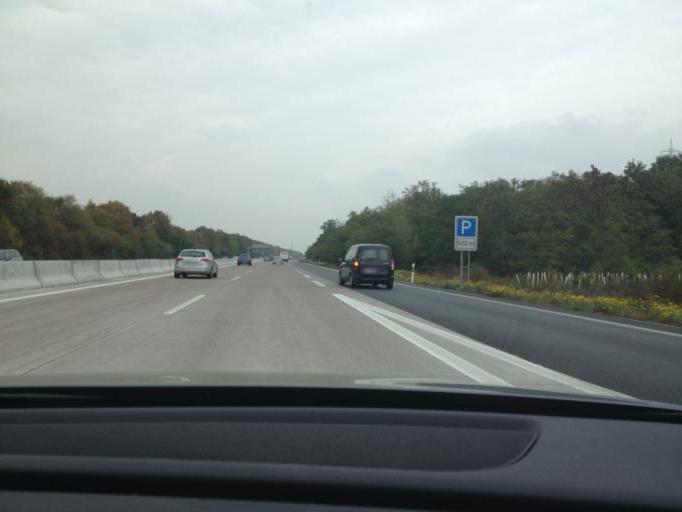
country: DE
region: Baden-Wuerttemberg
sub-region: Karlsruhe Region
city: Ketsch
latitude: 49.3646
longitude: 8.5461
